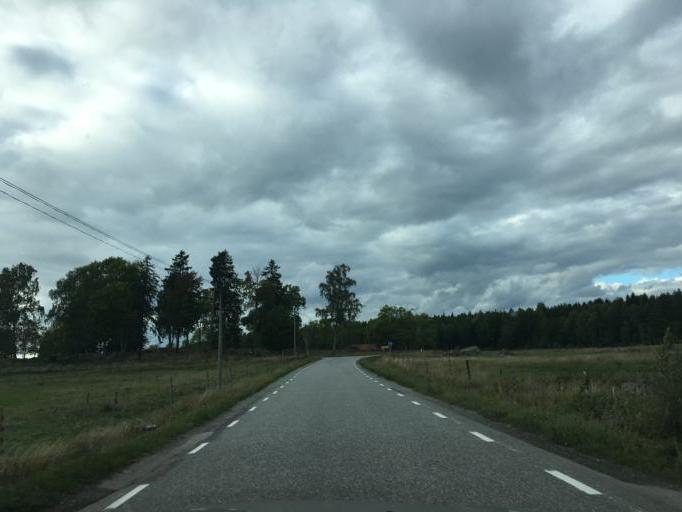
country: SE
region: Vaestmanland
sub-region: Vasteras
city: Tillberga
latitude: 59.5580
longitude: 16.7502
